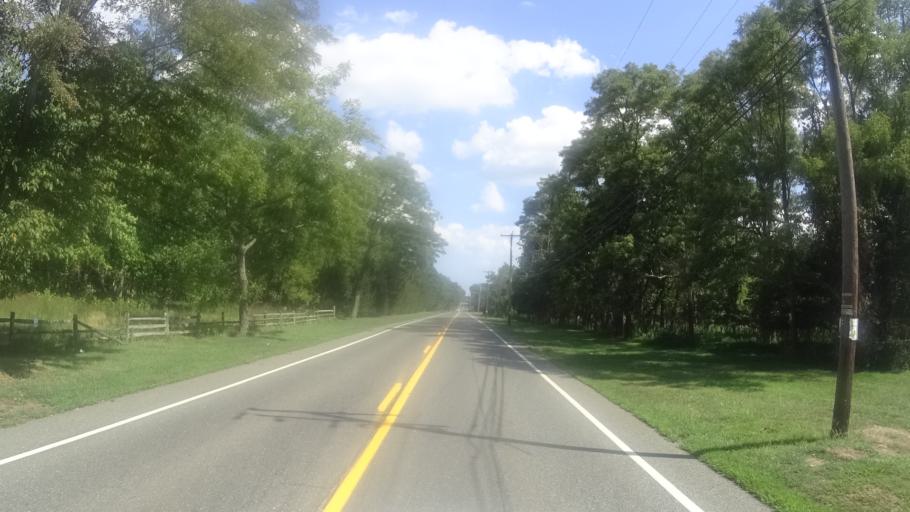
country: US
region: New Jersey
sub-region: Monmouth County
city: Ramtown
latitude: 40.1591
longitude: -74.1233
